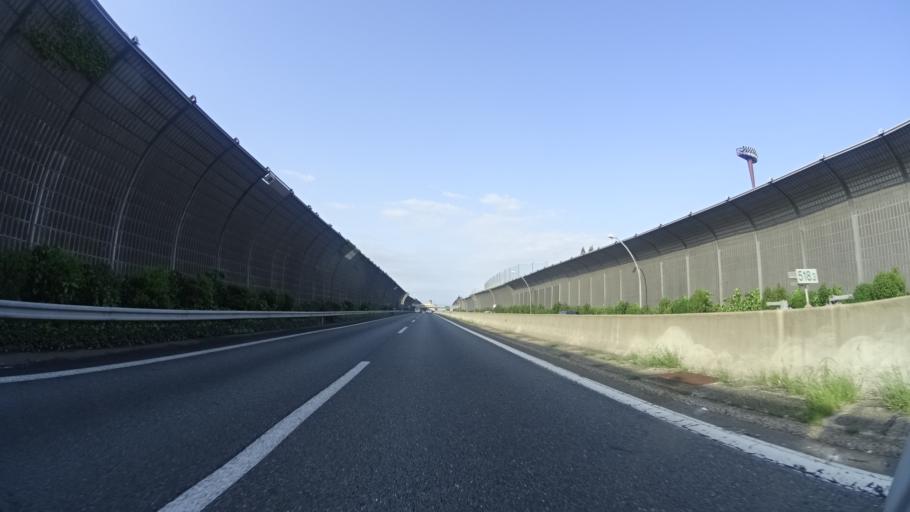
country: JP
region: Osaka
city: Suita
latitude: 34.7793
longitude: 135.5235
